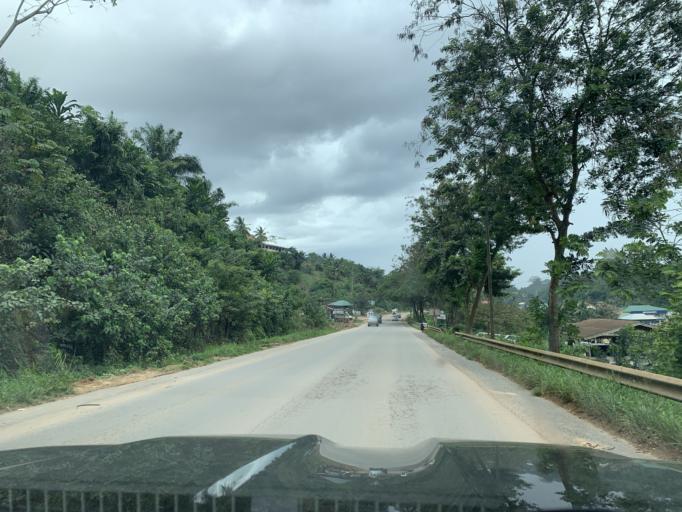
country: GH
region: Western
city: Tarkwa
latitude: 5.3231
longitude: -1.9841
